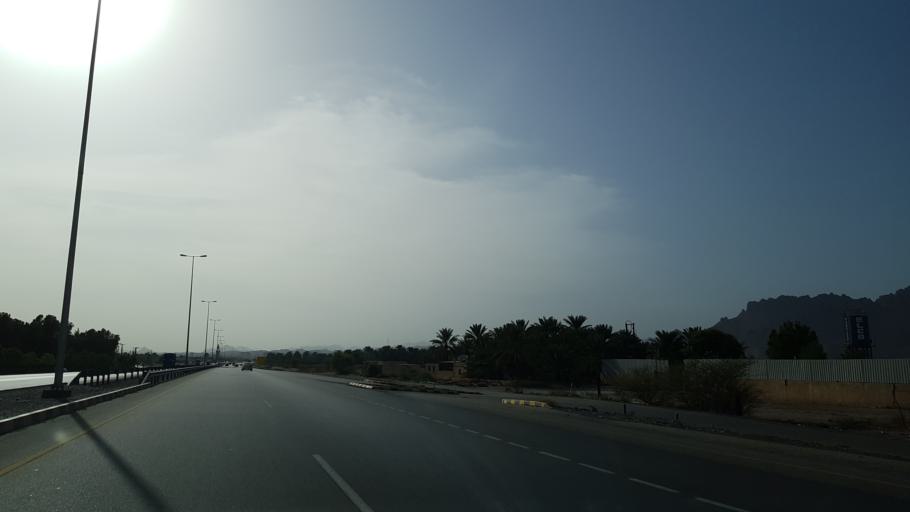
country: OM
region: Muhafazat ad Dakhiliyah
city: Nizwa
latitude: 22.8589
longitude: 57.5617
